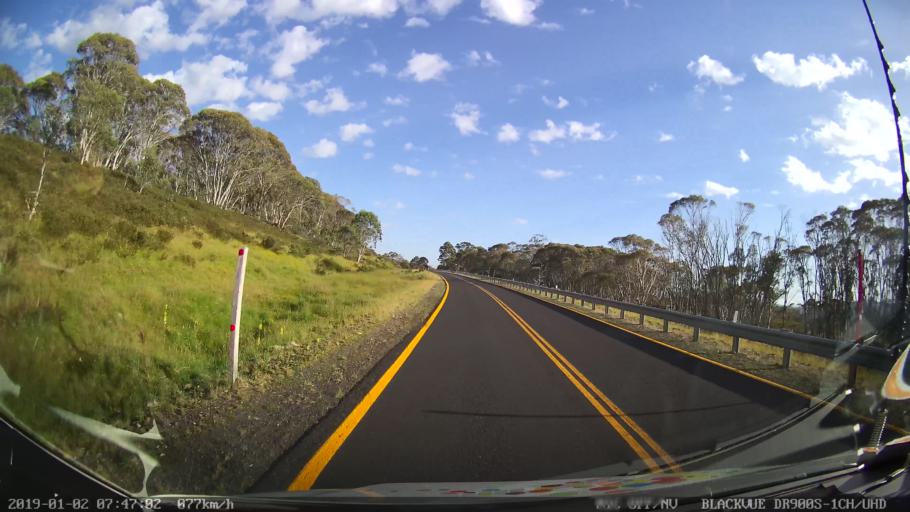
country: AU
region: New South Wales
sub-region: Tumut Shire
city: Tumut
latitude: -35.7692
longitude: 148.5215
